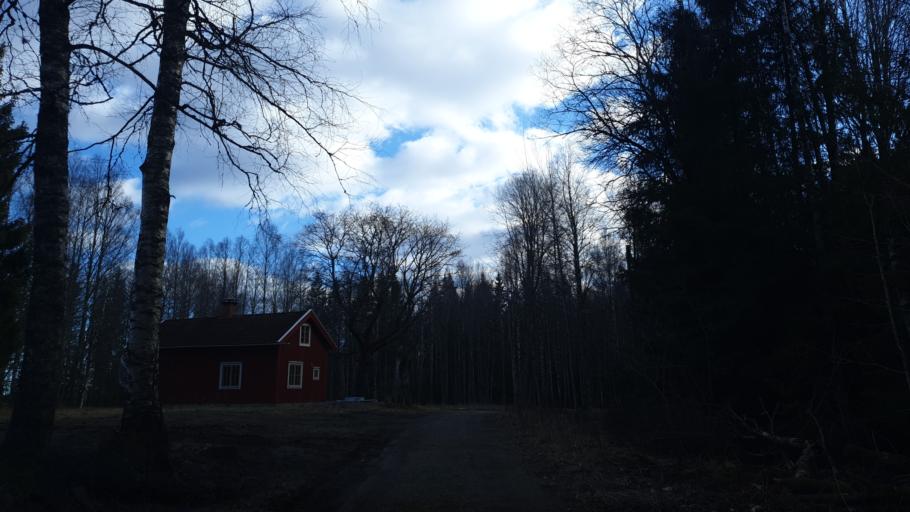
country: SE
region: OErebro
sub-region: Orebro Kommun
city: Garphyttan
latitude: 59.3693
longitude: 14.9678
